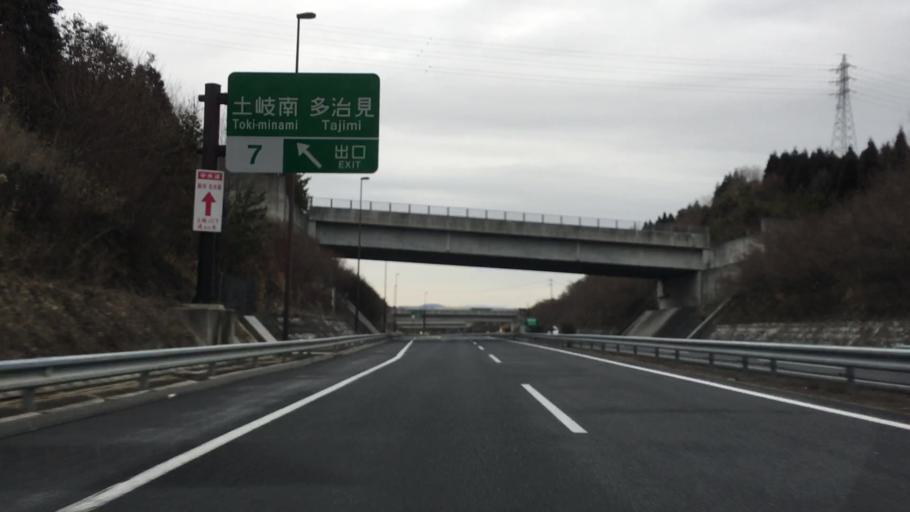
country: JP
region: Gifu
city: Toki
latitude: 35.3293
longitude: 137.1755
